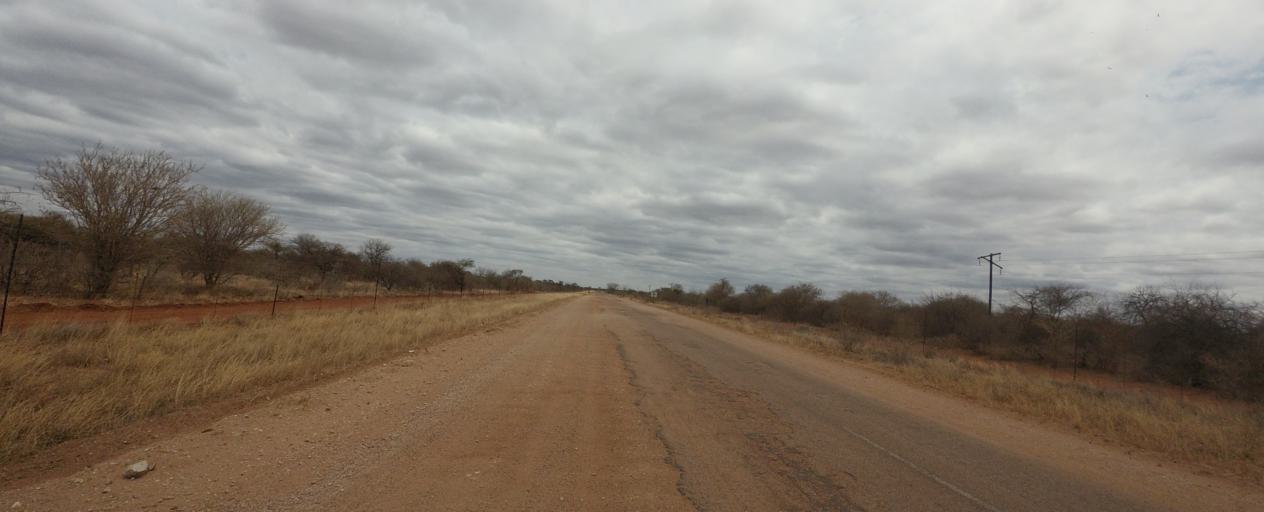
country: BW
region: Central
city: Mathathane
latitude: -22.7137
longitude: 28.5594
